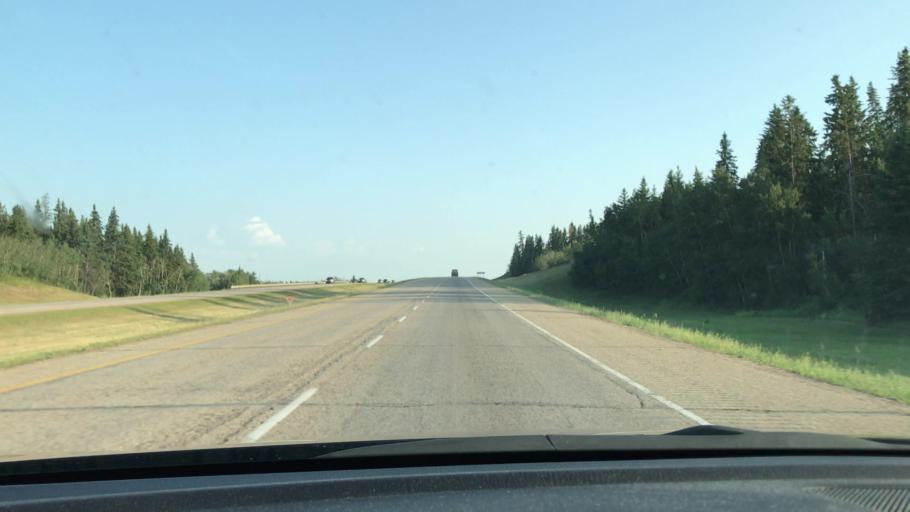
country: CA
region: Alberta
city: Ponoka
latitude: 52.5952
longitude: -113.6634
